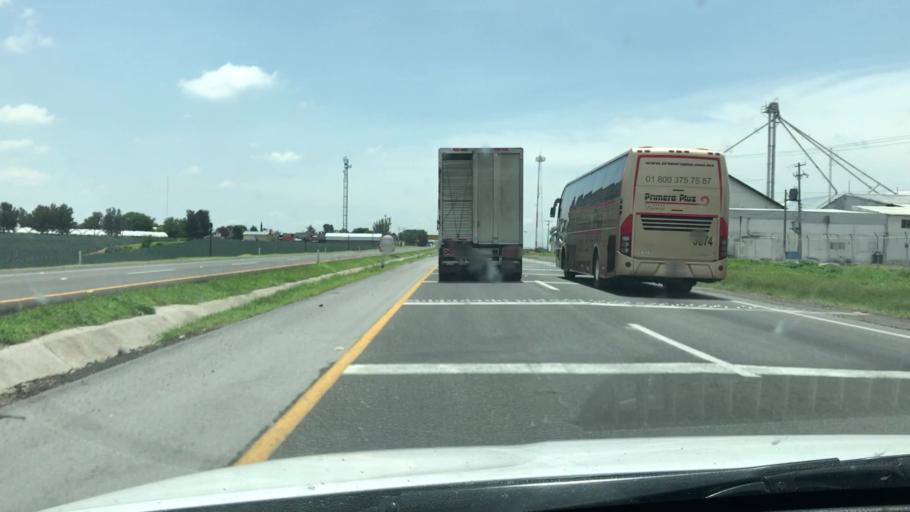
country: MX
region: Guanajuato
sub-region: Penjamo
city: Mezquite de Luna
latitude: 20.3787
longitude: -101.8409
